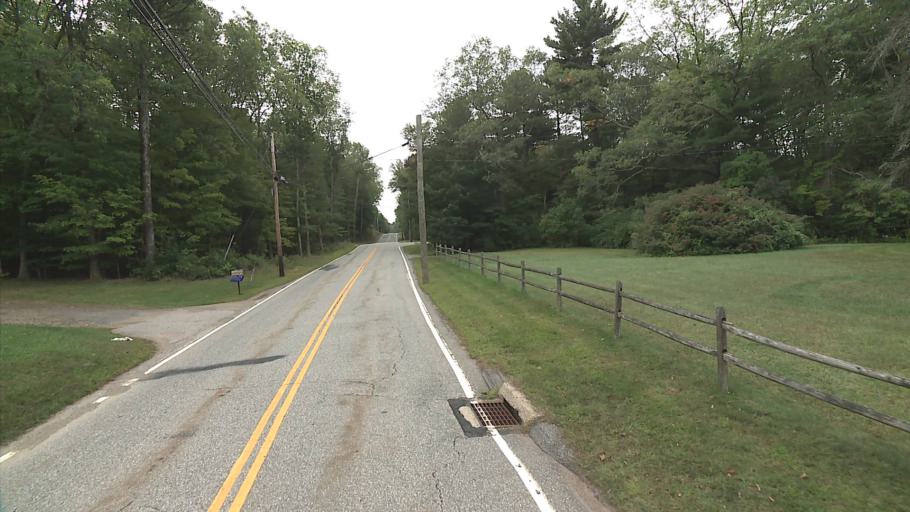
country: US
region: Connecticut
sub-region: Tolland County
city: Stafford Springs
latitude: 41.8888
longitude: -72.2678
